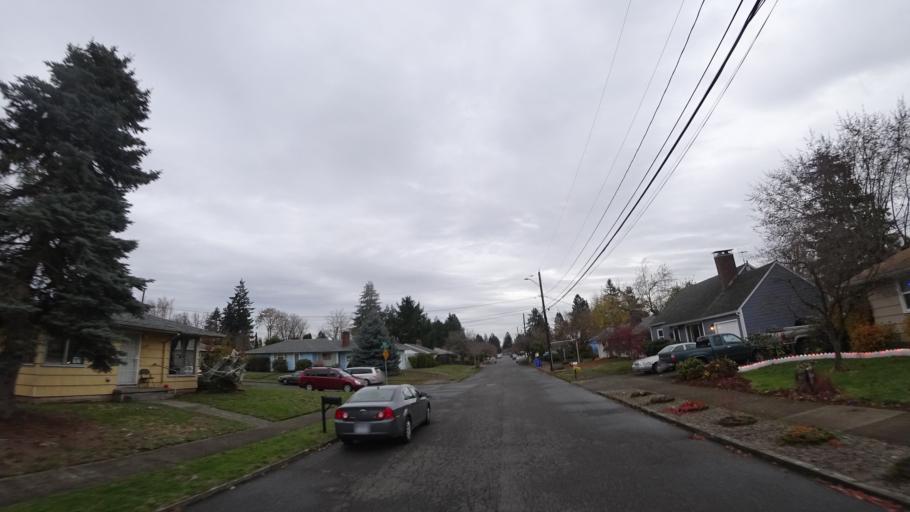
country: US
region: Oregon
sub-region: Multnomah County
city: Lents
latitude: 45.5147
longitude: -122.5369
